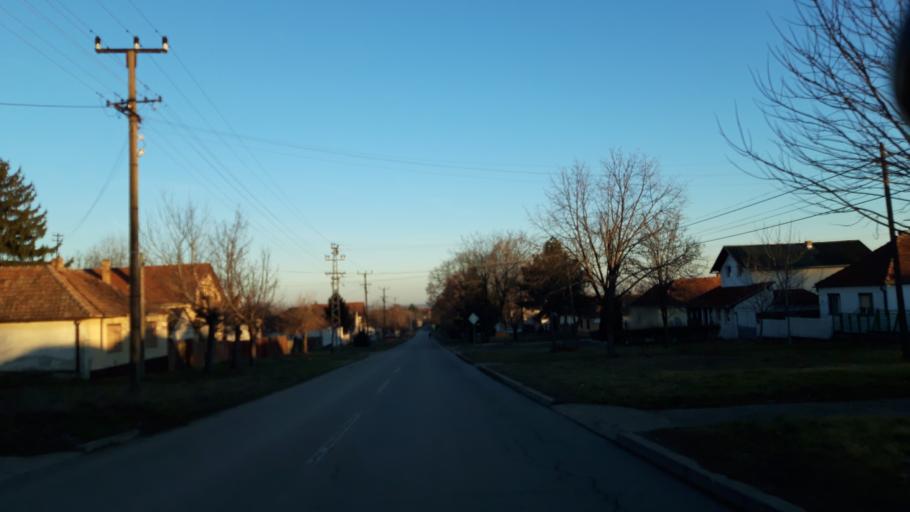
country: RS
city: Cortanovci
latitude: 45.1578
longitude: 20.0116
